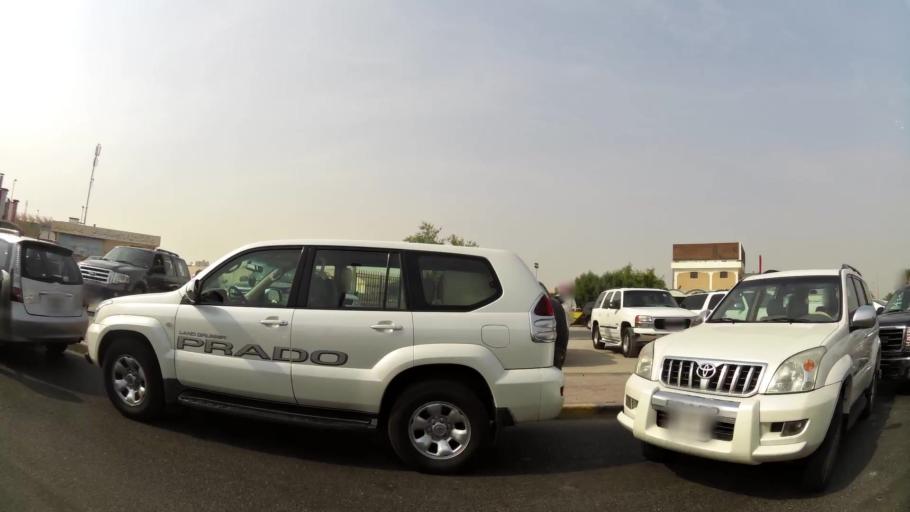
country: KW
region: Al Asimah
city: Ar Rabiyah
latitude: 29.2860
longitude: 47.9422
